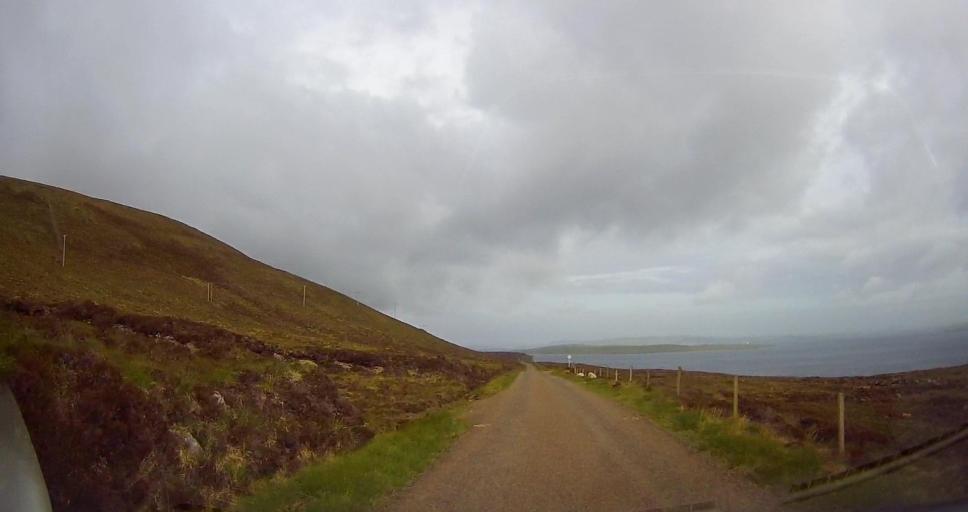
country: GB
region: Scotland
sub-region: Orkney Islands
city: Stromness
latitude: 58.8858
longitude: -3.2506
